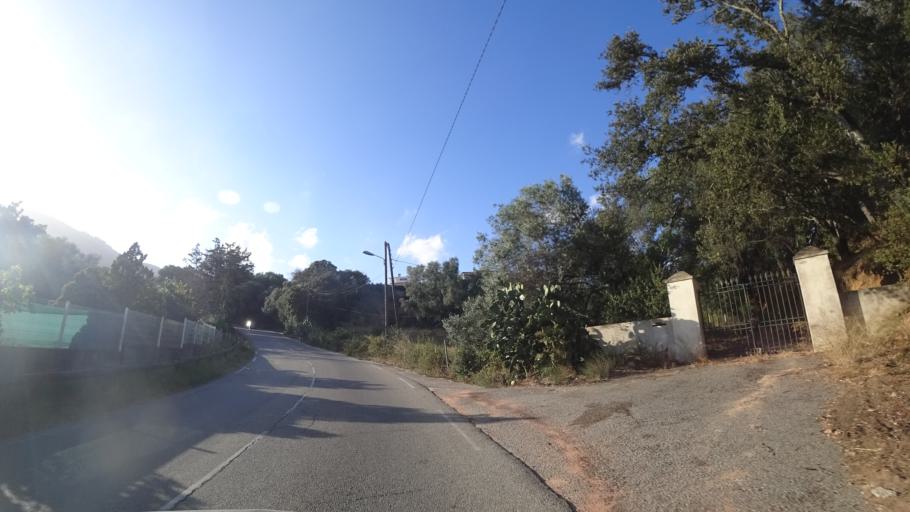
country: FR
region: Corsica
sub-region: Departement de la Corse-du-Sud
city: Ajaccio
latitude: 41.9472
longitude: 8.7366
